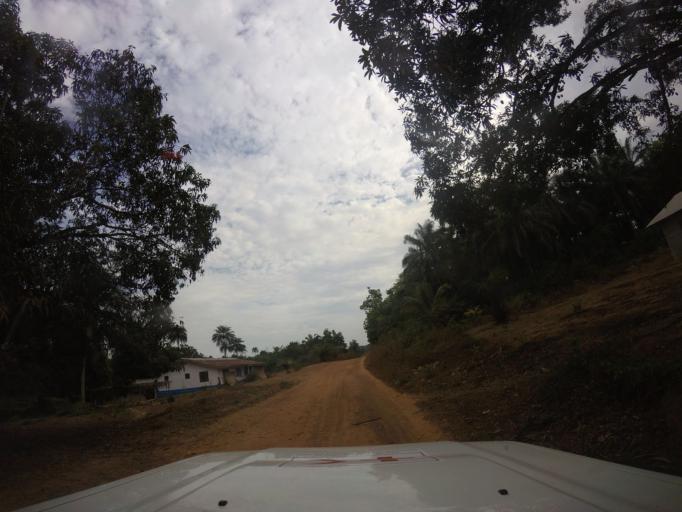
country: LR
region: Grand Cape Mount
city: Robertsport
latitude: 6.9974
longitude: -11.2964
